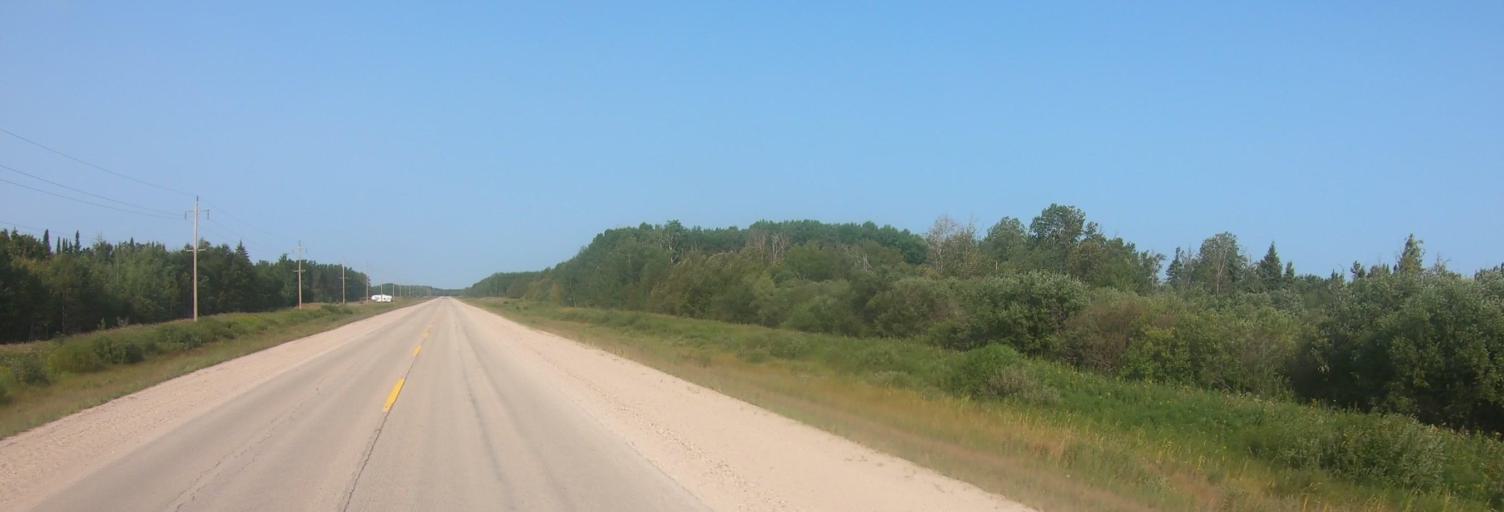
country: US
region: Minnesota
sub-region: Roseau County
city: Roseau
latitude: 49.0234
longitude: -95.7138
